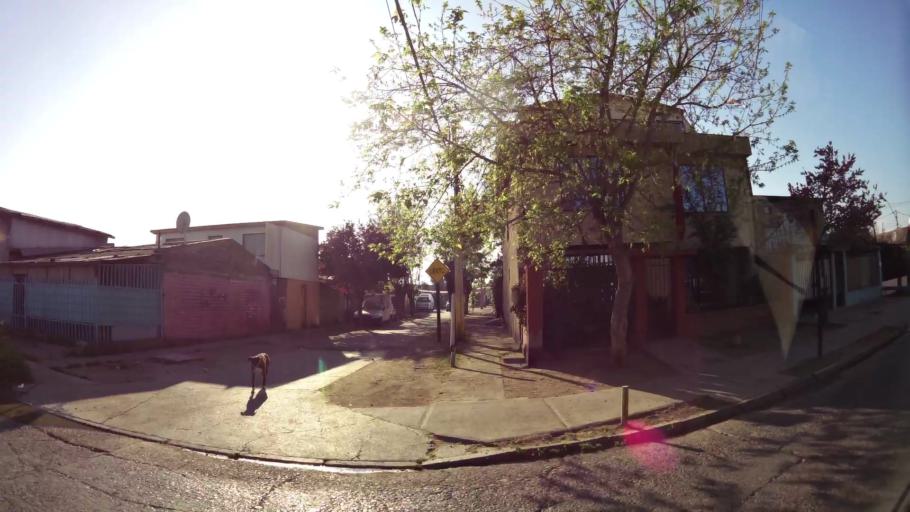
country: CL
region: Santiago Metropolitan
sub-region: Provincia de Santiago
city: Santiago
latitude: -33.3747
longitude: -70.6694
